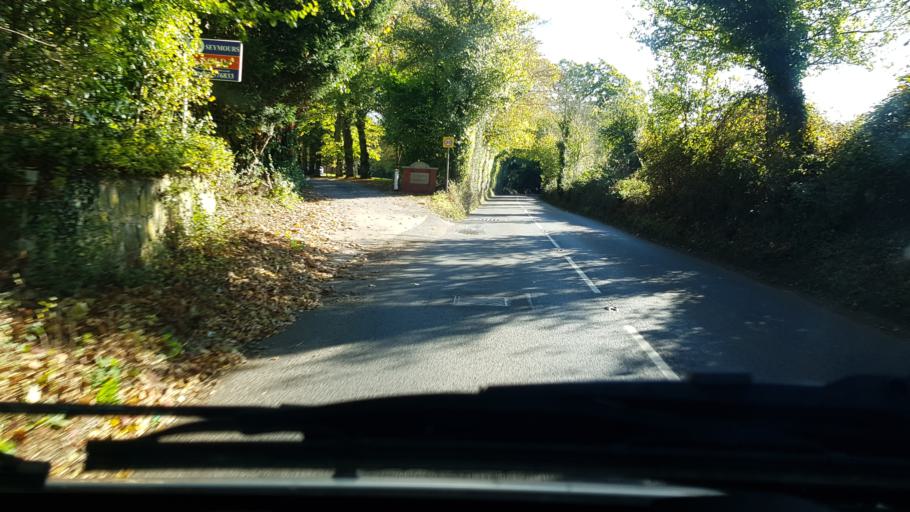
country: GB
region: England
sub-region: Surrey
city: Chilworth
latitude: 51.1955
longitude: -0.5375
